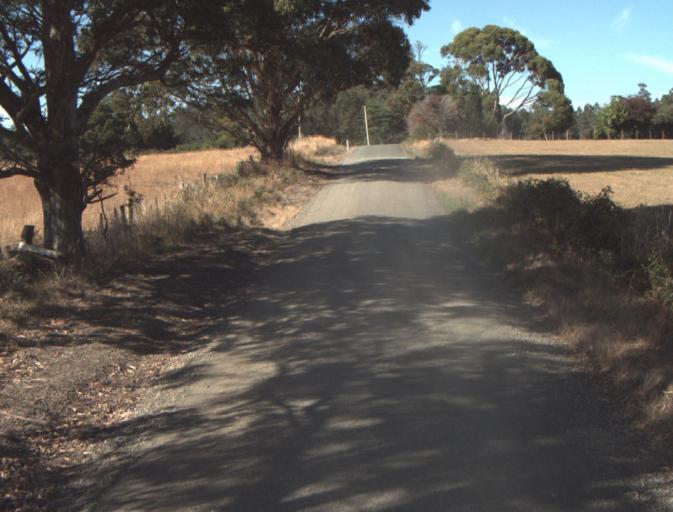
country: AU
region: Tasmania
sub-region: Launceston
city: Mayfield
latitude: -41.1769
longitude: 147.2157
